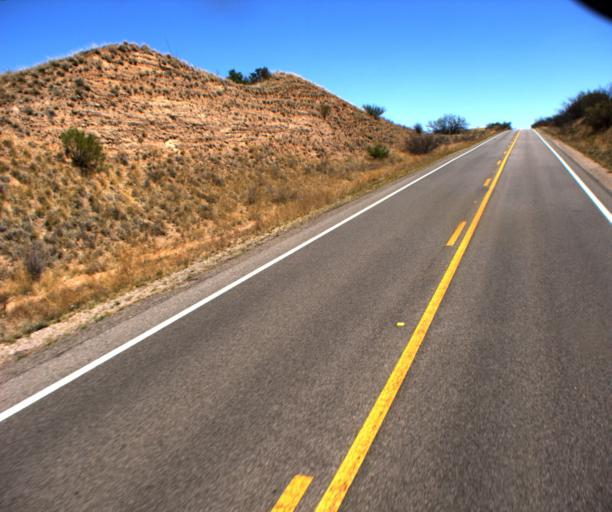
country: US
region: Arizona
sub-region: Pima County
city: Corona de Tucson
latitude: 31.7775
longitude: -110.6895
